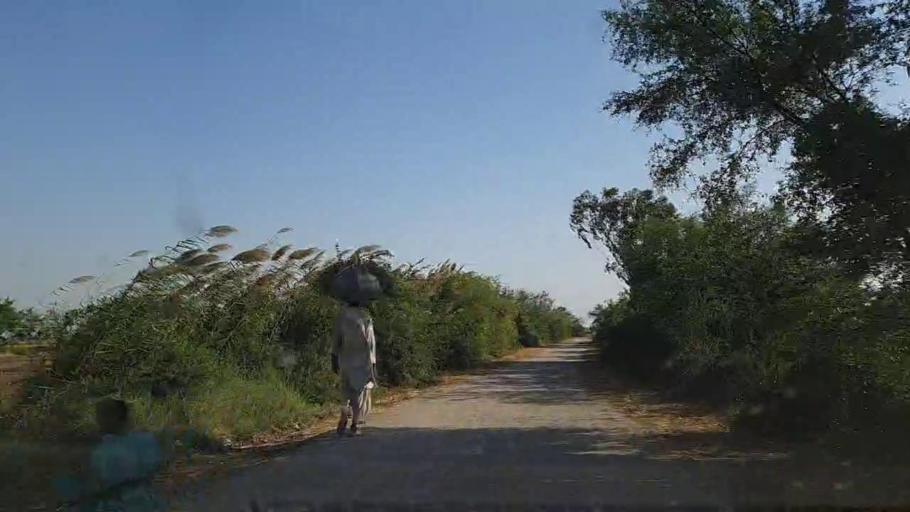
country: PK
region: Sindh
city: Daro Mehar
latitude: 24.6327
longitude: 68.0777
